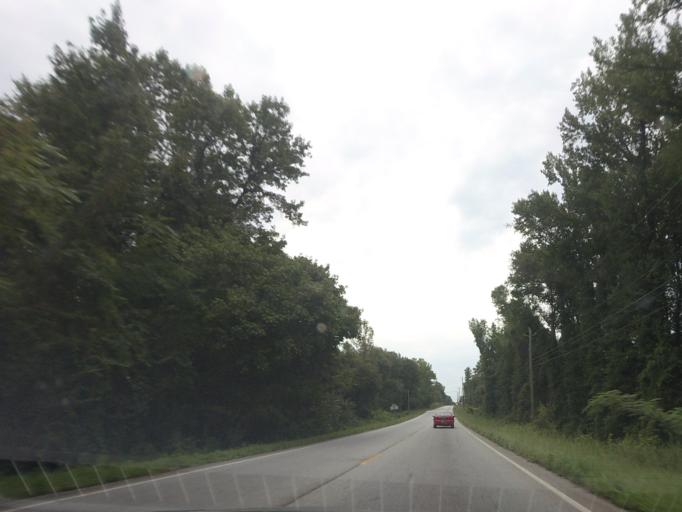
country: US
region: Georgia
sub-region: Bibb County
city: Macon
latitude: 32.8206
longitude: -83.5263
